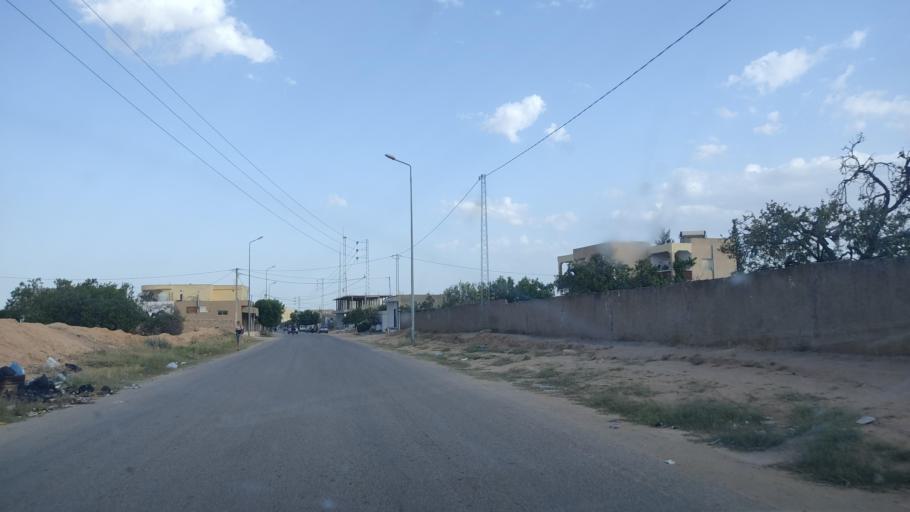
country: TN
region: Safaqis
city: Sfax
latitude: 34.8471
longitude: 10.6150
